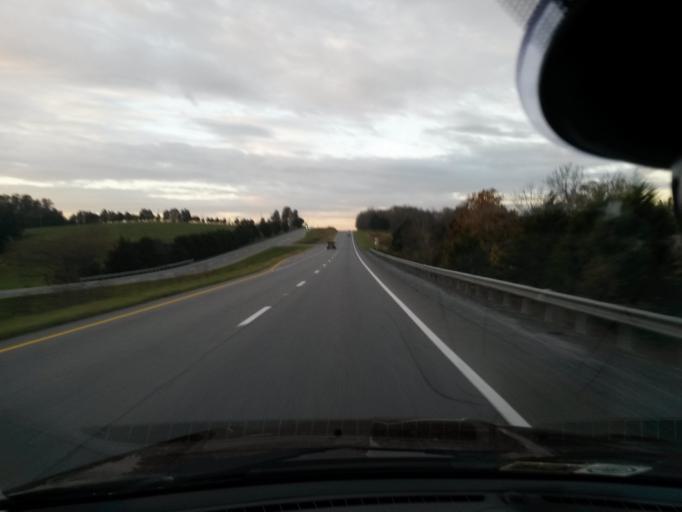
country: US
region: Virginia
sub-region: Botetourt County
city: Fincastle
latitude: 37.5439
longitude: -79.8609
